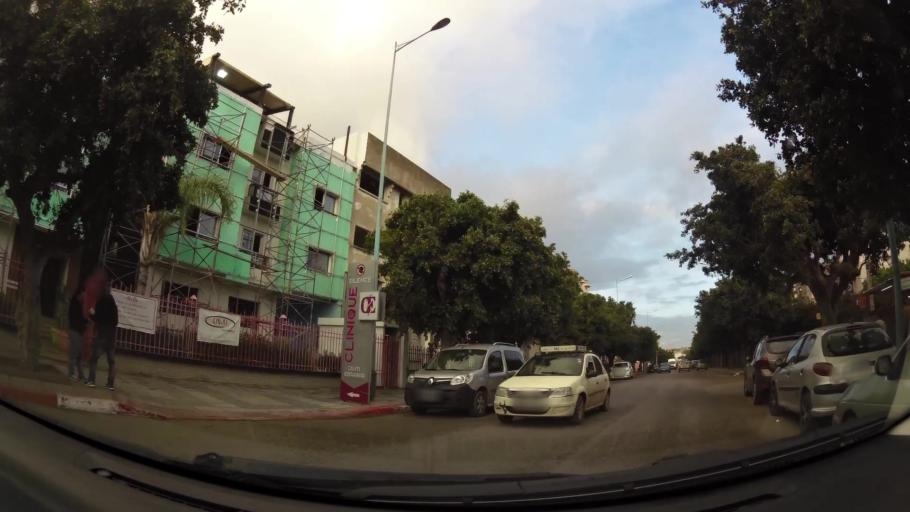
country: MA
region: Doukkala-Abda
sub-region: El-Jadida
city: El Jadida
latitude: 33.2434
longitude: -8.5018
